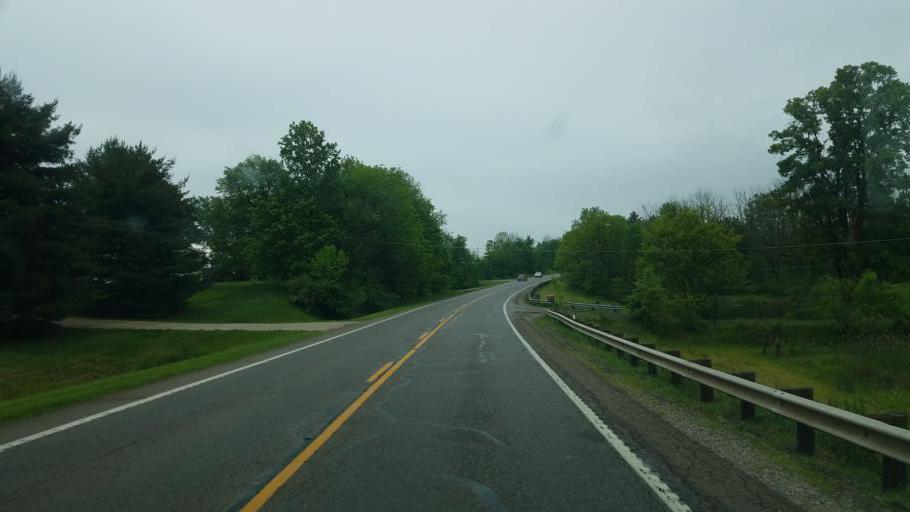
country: US
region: Ohio
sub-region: Morrow County
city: Mount Gilead
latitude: 40.5460
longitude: -82.7992
